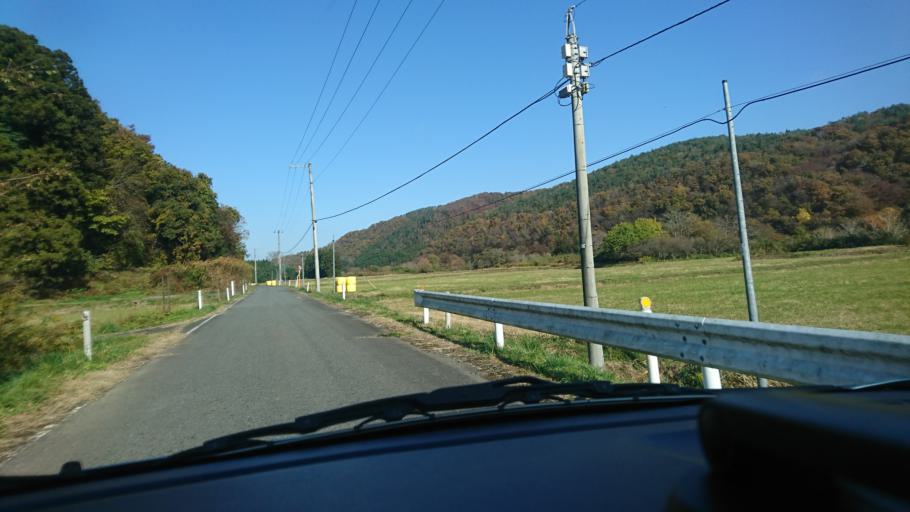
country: JP
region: Iwate
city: Ichinoseki
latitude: 38.8114
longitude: 141.2479
